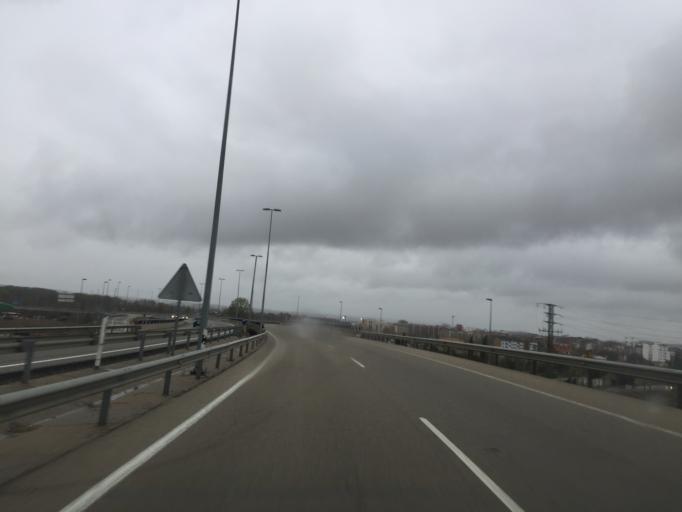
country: ES
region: Castille and Leon
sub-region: Provincia de Leon
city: Leon
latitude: 42.5747
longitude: -5.5517
